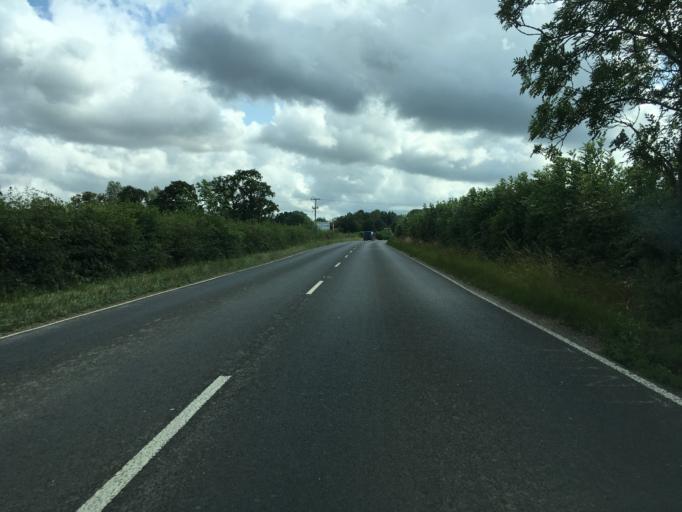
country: GB
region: England
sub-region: Kent
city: Tenterden
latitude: 51.1082
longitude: 0.6452
